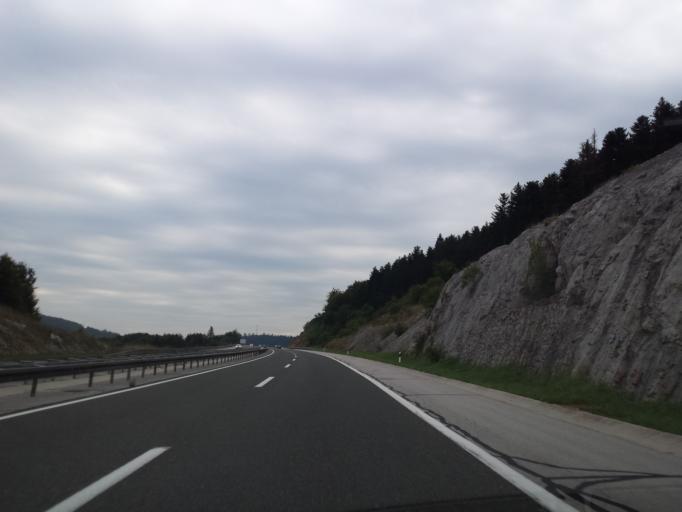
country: HR
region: Licko-Senjska
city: Otocac
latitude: 44.8593
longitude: 15.2146
